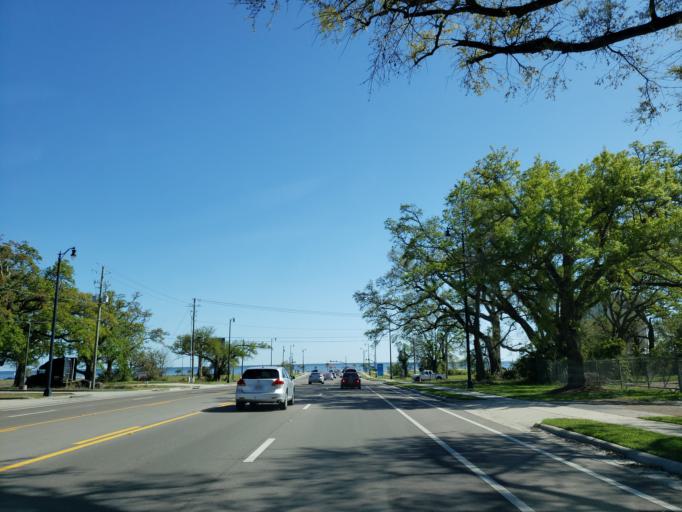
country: US
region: Mississippi
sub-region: Harrison County
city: Gulfport
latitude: 30.3851
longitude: -89.0270
